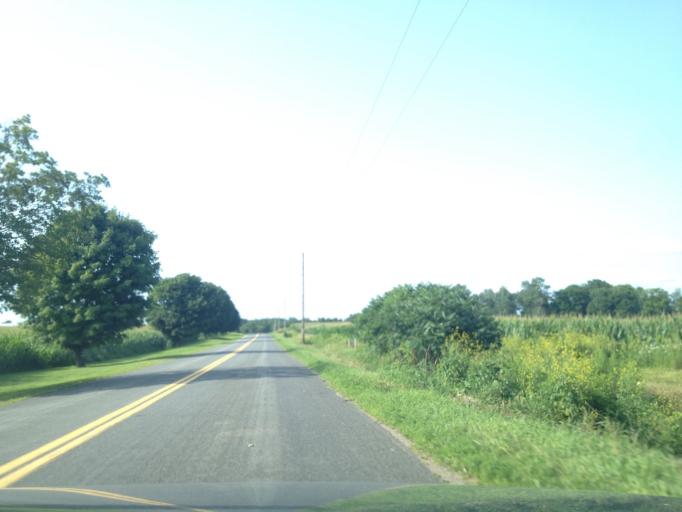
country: CA
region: Ontario
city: Aylmer
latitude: 42.7399
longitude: -80.8532
